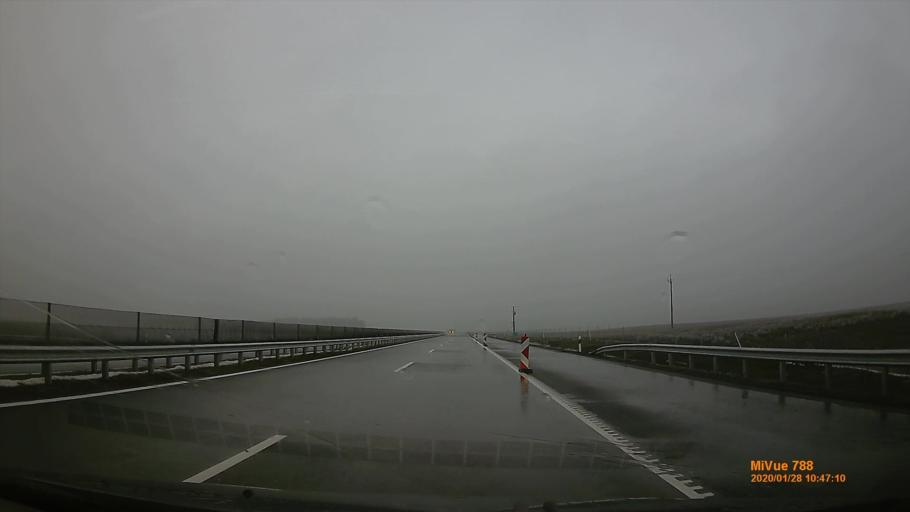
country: HU
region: Pest
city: Monor
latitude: 47.3717
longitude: 19.4752
